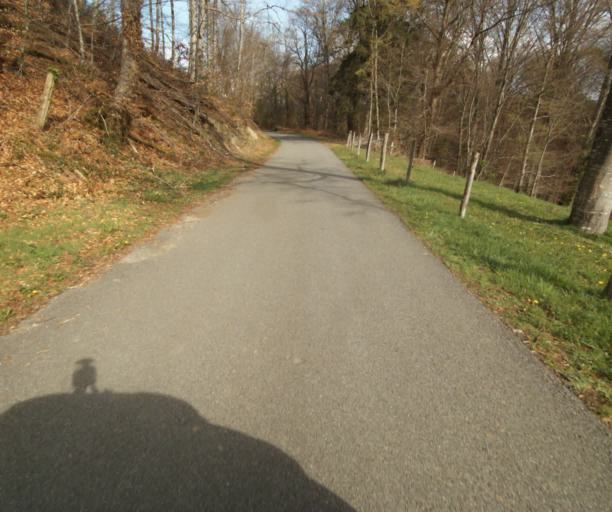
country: FR
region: Limousin
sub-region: Departement de la Correze
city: Correze
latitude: 45.3407
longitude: 1.8573
